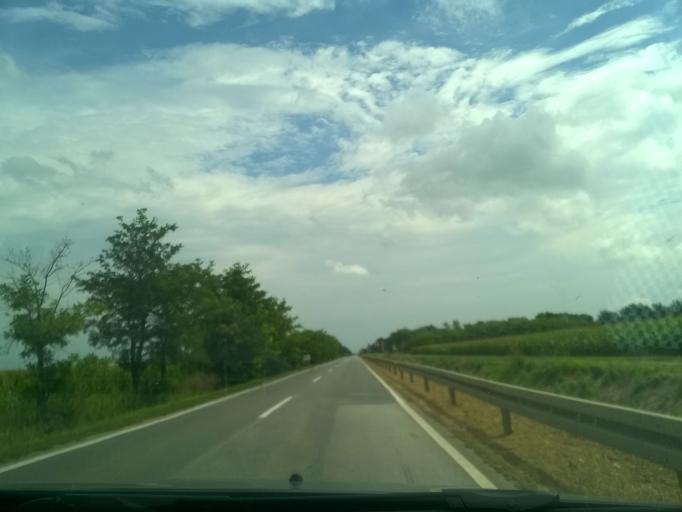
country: RS
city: Lazarevo
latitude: 45.3900
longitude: 20.5760
